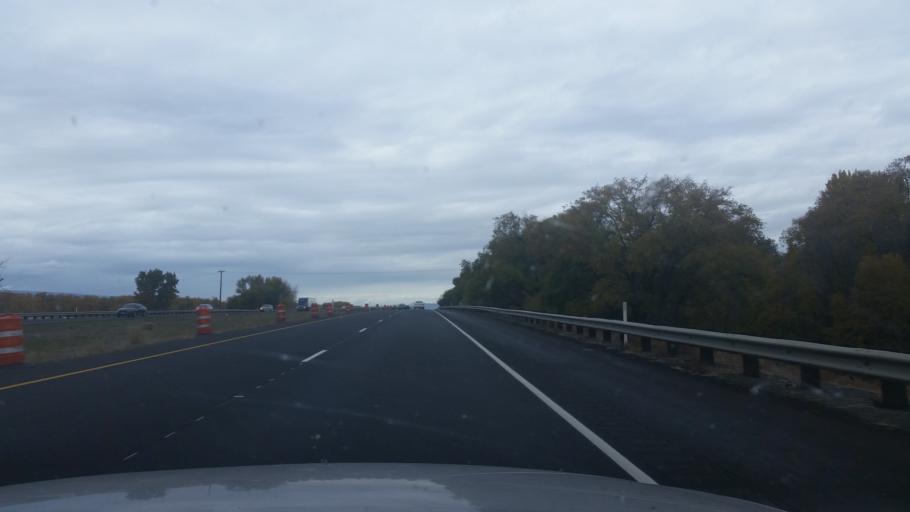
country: US
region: Washington
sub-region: Kittitas County
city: Ellensburg
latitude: 46.9793
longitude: -120.5580
